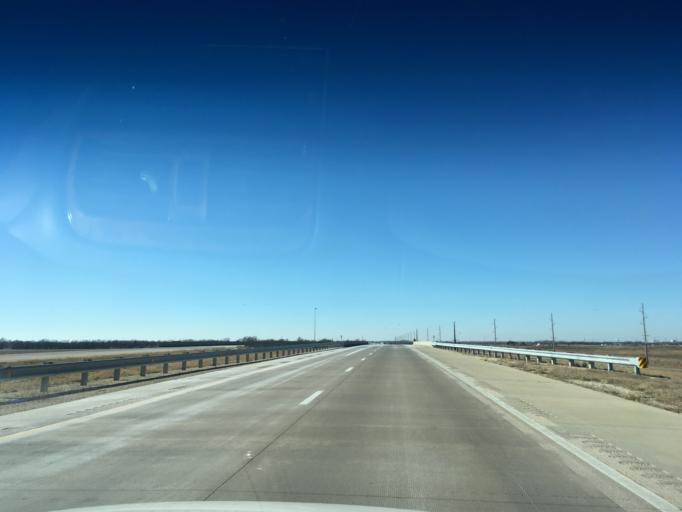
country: US
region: Kansas
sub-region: Reno County
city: Hutchinson
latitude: 38.0288
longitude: -97.8650
